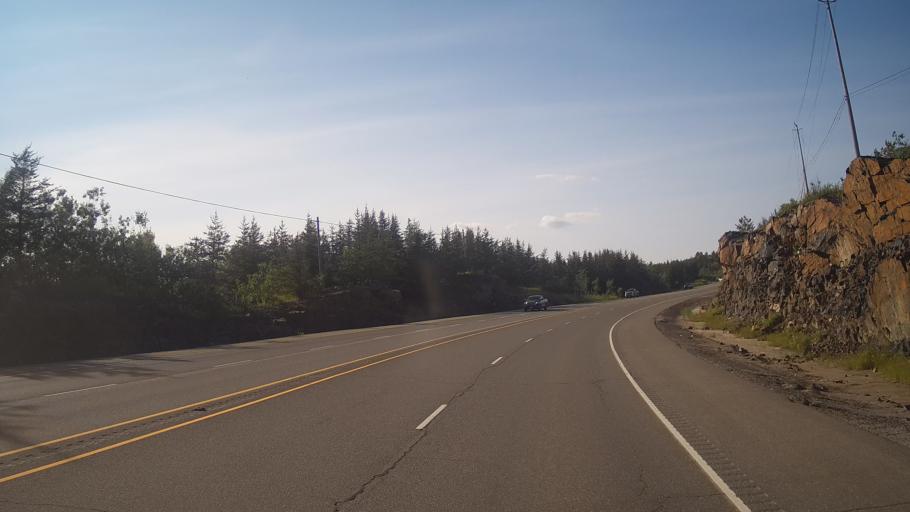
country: CA
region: Ontario
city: Greater Sudbury
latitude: 46.5090
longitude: -81.0514
